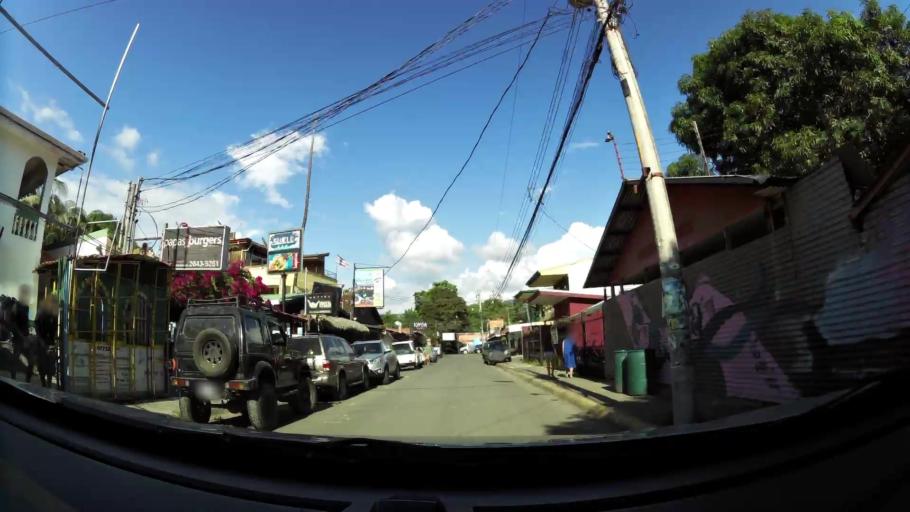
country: CR
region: Puntarenas
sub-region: Canton de Garabito
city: Jaco
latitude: 9.6146
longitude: -84.6293
